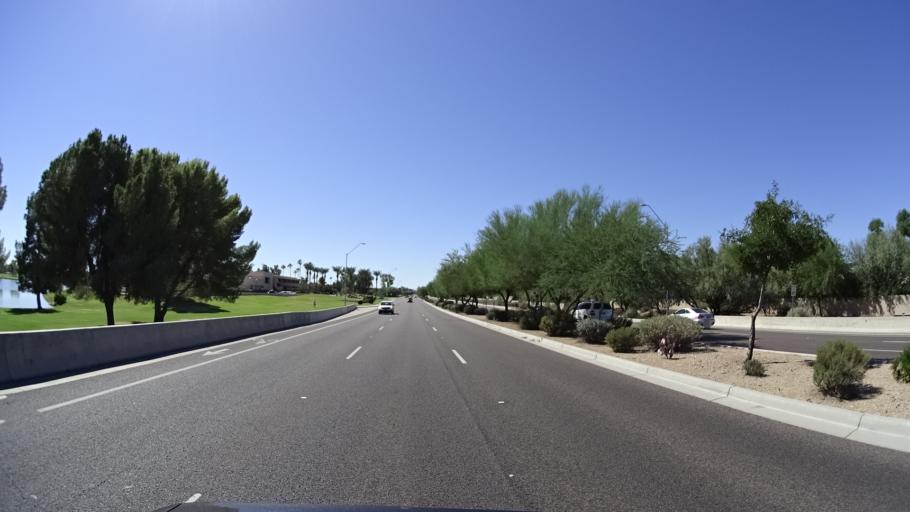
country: US
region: Arizona
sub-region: Maricopa County
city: Paradise Valley
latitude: 33.5499
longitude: -111.9259
